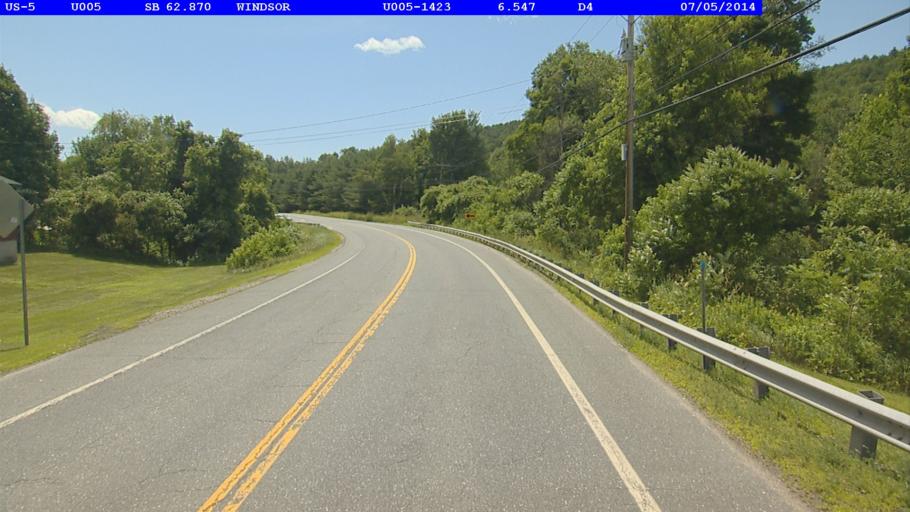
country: US
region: Vermont
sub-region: Windsor County
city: Windsor
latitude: 43.5164
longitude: -72.4039
